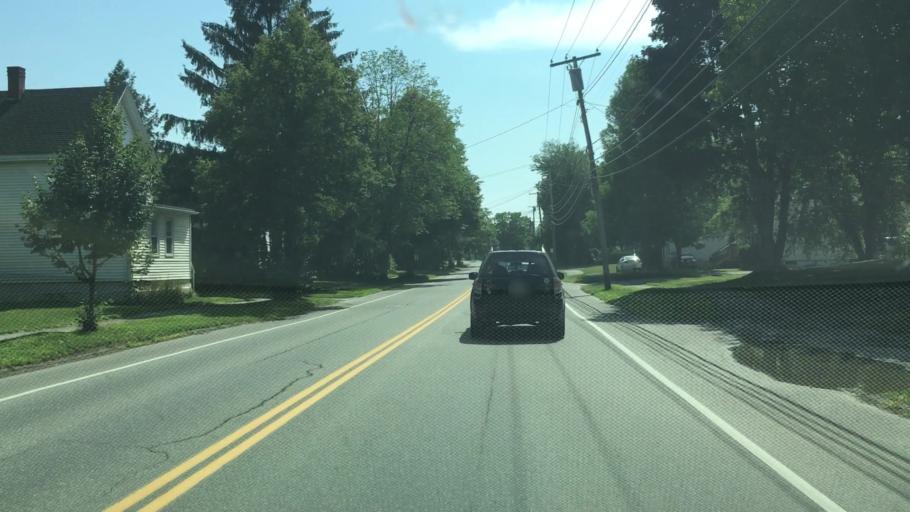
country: US
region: Maine
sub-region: Penobscot County
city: Brewer
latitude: 44.8178
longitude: -68.7639
